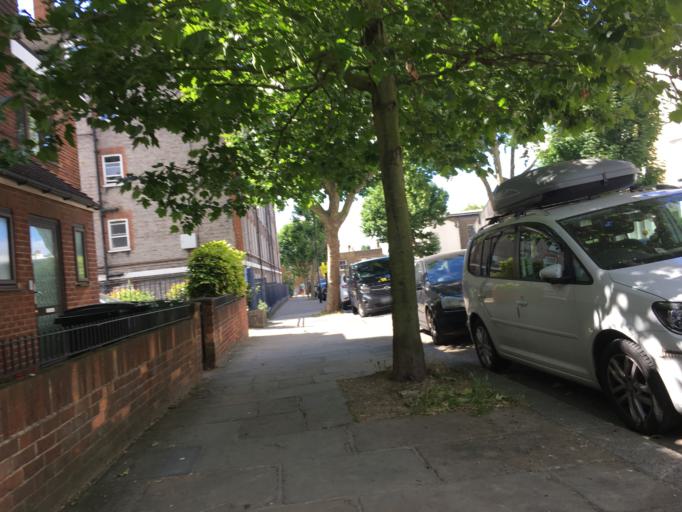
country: GB
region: England
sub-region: Greater London
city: Camden Town
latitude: 51.5517
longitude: -0.1377
